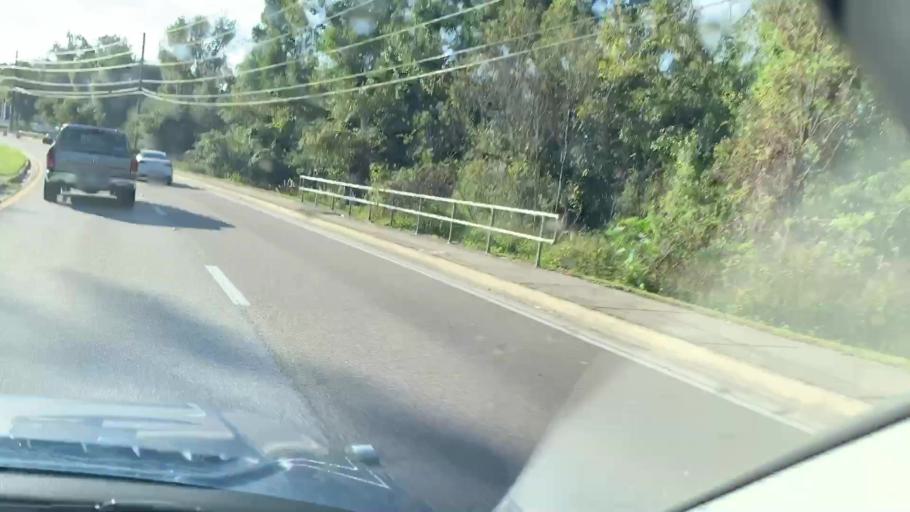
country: US
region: Florida
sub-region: Polk County
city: Gibsonia
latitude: 28.0771
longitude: -81.9932
